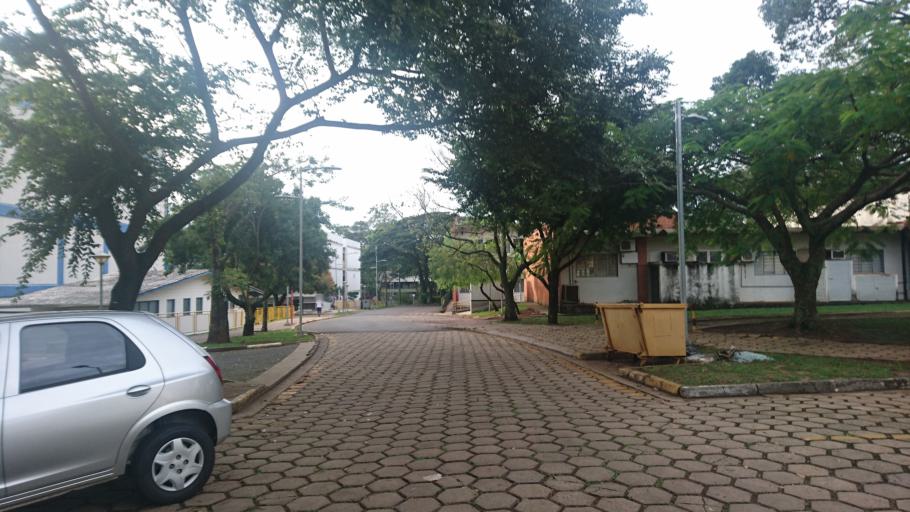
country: BR
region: Sao Paulo
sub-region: Sao Carlos
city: Sao Carlos
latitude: -22.0101
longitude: -47.8963
